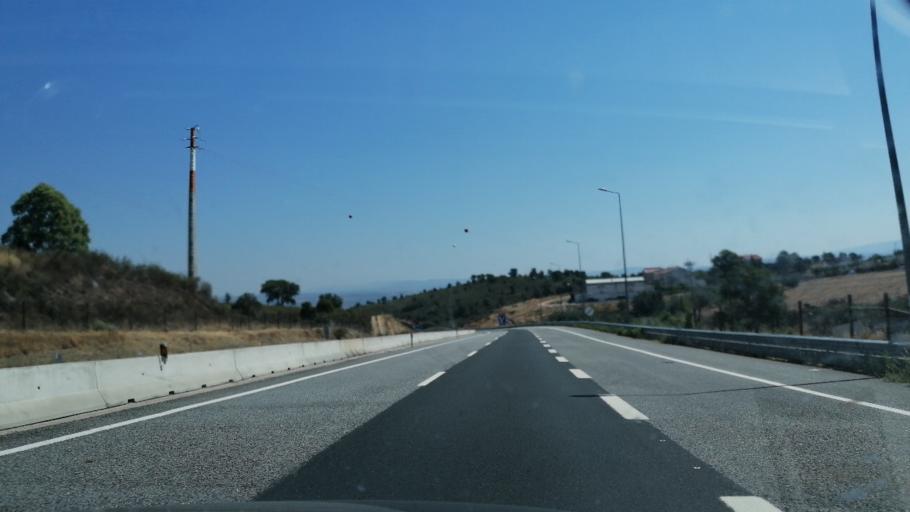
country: PT
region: Braganca
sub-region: Mirandela
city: Mirandela
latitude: 41.4802
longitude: -7.2160
